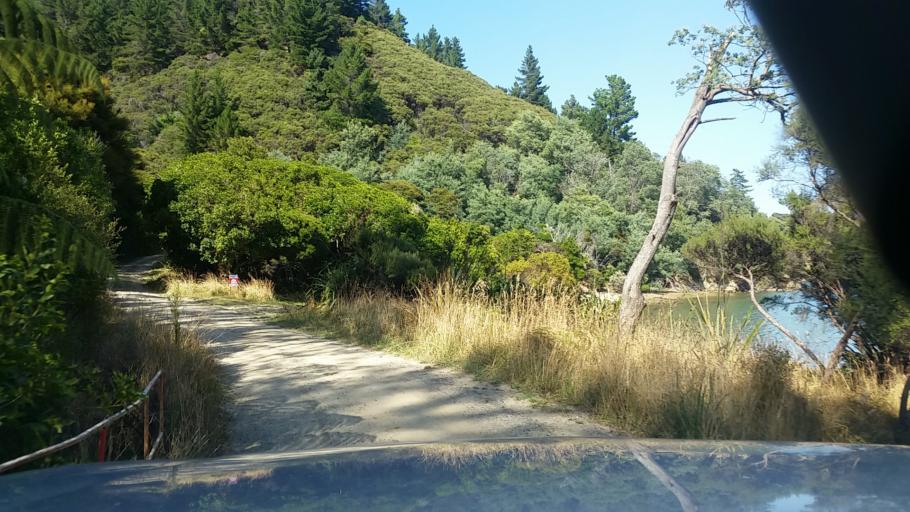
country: NZ
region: Marlborough
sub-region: Marlborough District
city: Picton
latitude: -41.3036
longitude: 174.1779
